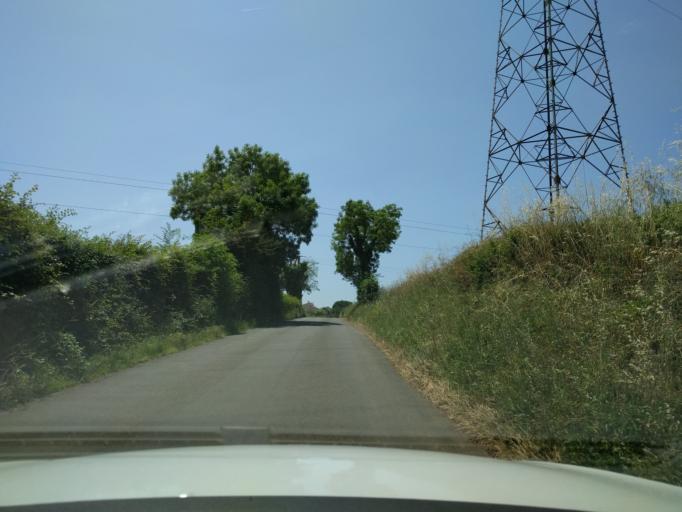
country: FR
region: Poitou-Charentes
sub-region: Departement des Deux-Sevres
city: Niort
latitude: 46.3537
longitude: -0.4575
